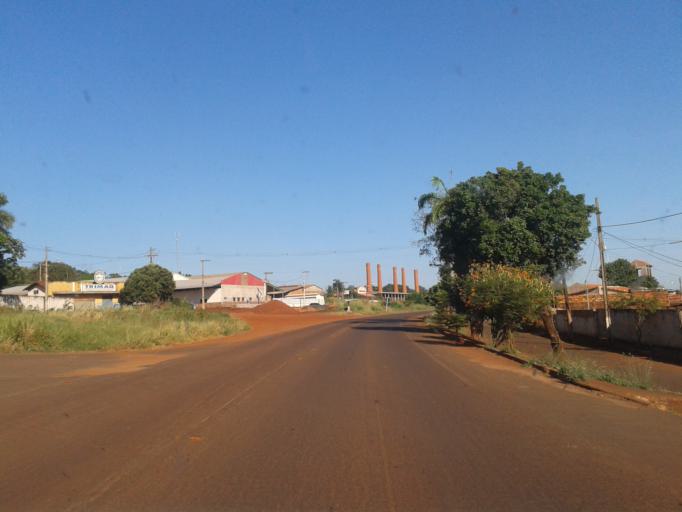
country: BR
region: Minas Gerais
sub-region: Capinopolis
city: Capinopolis
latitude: -18.6868
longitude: -49.5799
